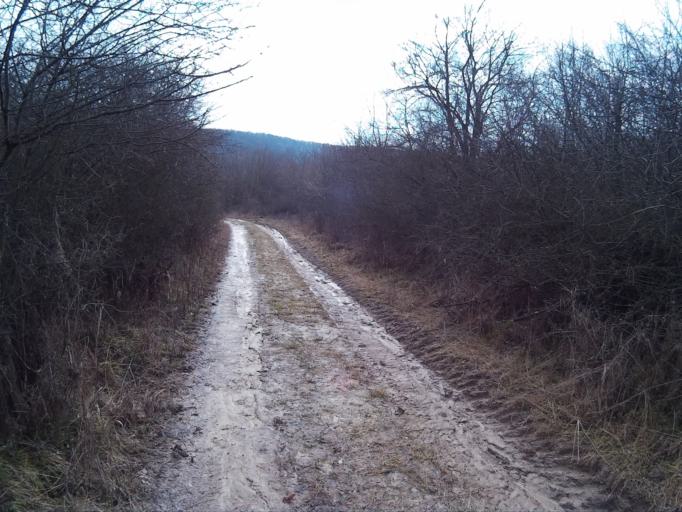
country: HU
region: Borsod-Abauj-Zemplen
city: Satoraljaujhely
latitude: 48.4042
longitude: 21.6019
